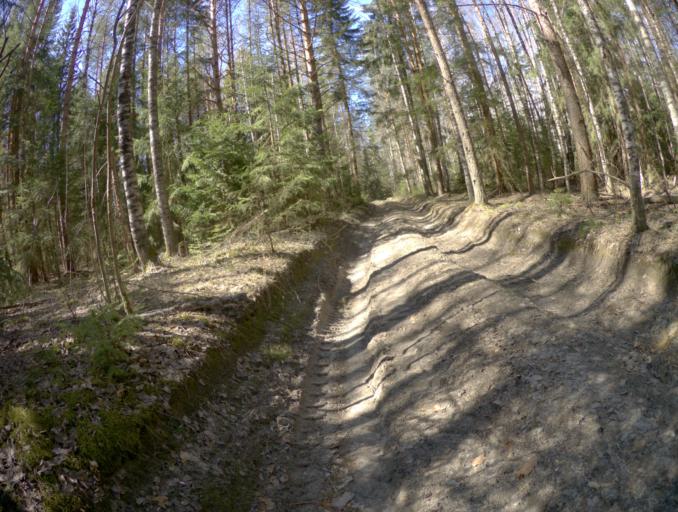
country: RU
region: Vladimir
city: Ivanishchi
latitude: 55.8385
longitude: 40.4431
